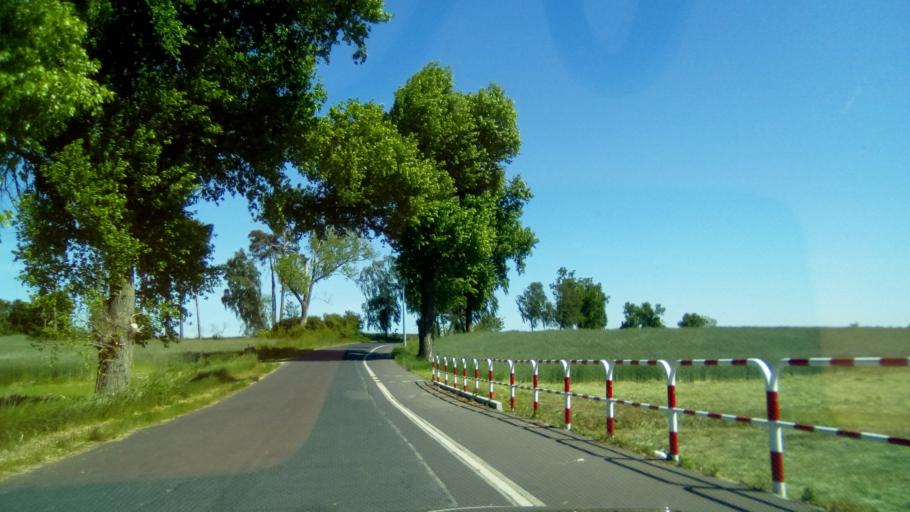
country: PL
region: Greater Poland Voivodeship
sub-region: Powiat gnieznienski
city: Gniezno
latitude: 52.4617
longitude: 17.5638
